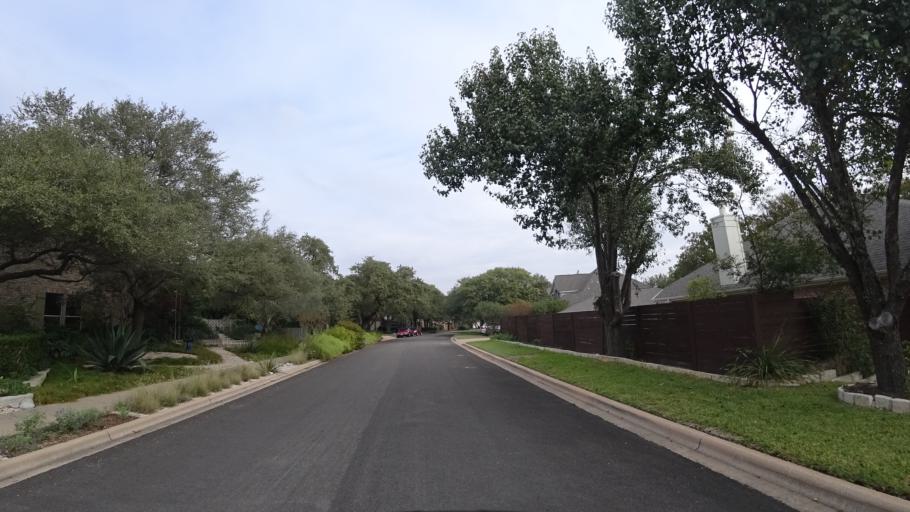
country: US
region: Texas
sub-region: Travis County
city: Shady Hollow
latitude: 30.1907
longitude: -97.8888
